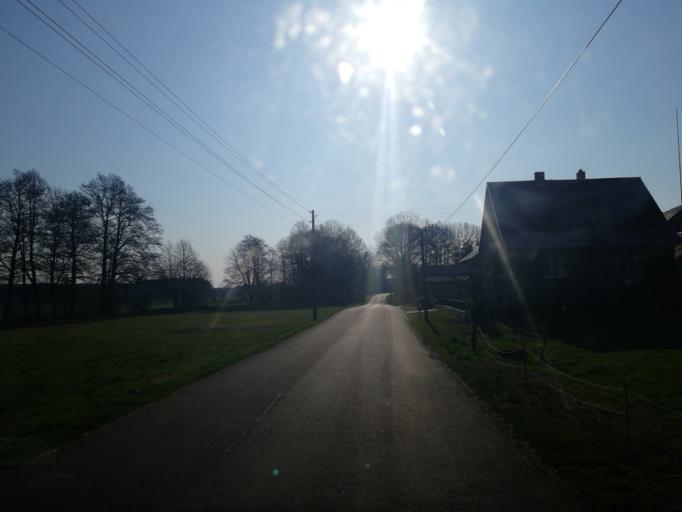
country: DE
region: Brandenburg
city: Drahnsdorf
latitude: 51.8970
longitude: 13.5578
